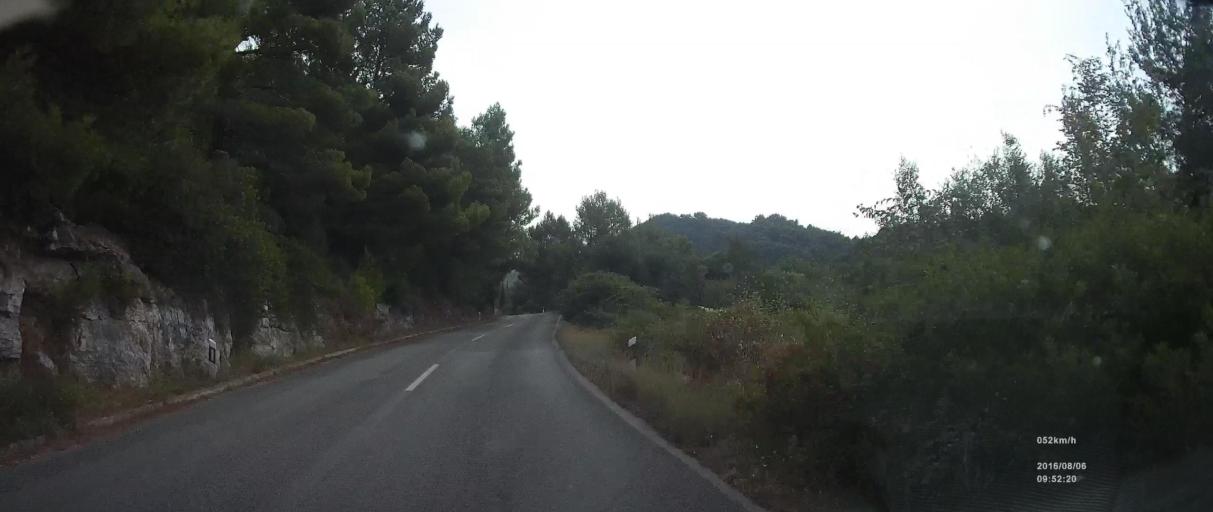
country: HR
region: Dubrovacko-Neretvanska
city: Blato
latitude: 42.7311
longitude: 17.5740
